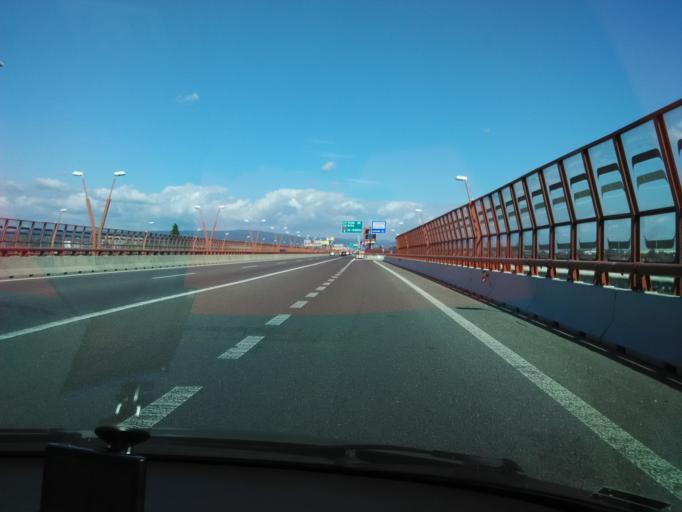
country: SK
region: Bratislavsky
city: Bratislava
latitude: 48.1491
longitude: 17.1811
